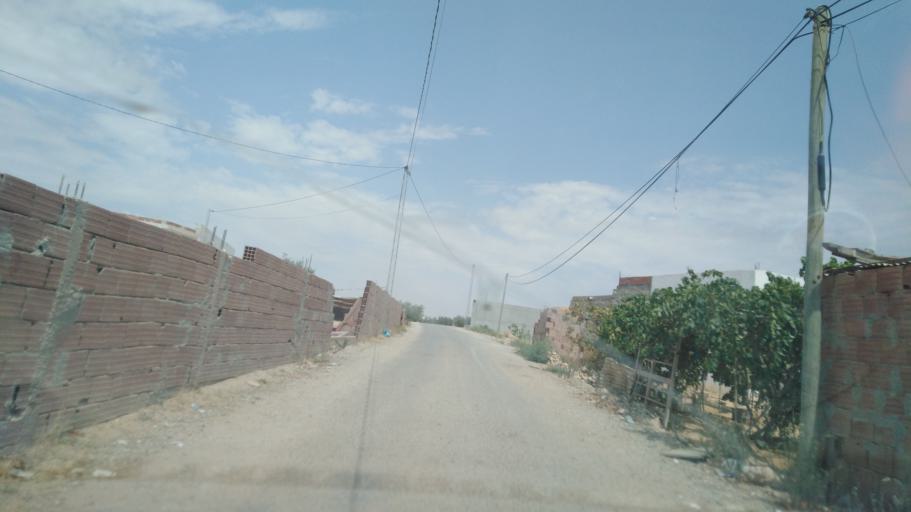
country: TN
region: Safaqis
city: Sfax
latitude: 34.7441
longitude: 10.5604
